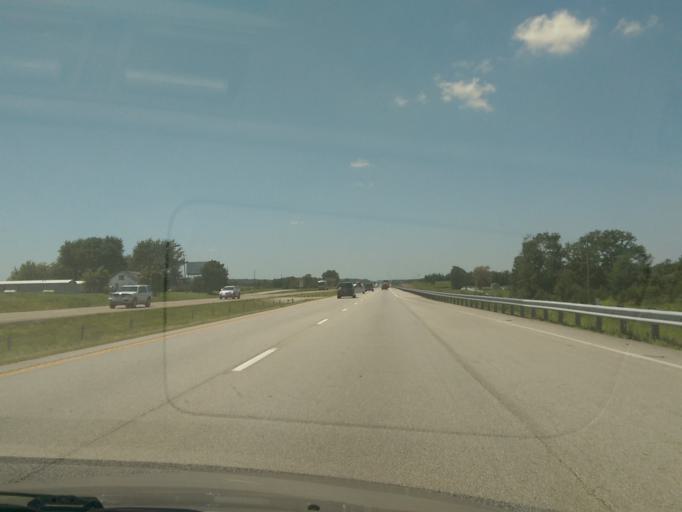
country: US
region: Missouri
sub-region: Cooper County
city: Boonville
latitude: 38.9353
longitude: -92.8518
